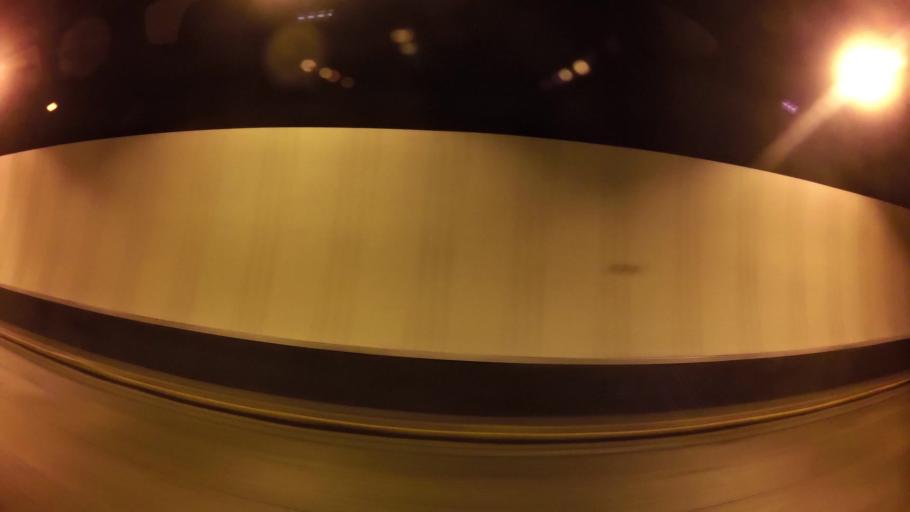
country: CL
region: Santiago Metropolitan
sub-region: Provincia de Santiago
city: Santiago
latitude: -33.4063
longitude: -70.6146
